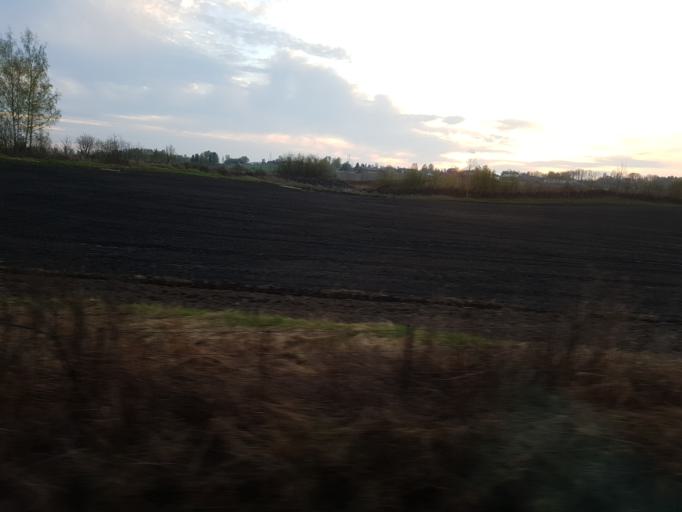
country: NO
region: Hedmark
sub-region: Hamar
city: Hamar
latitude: 60.7561
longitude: 11.1116
